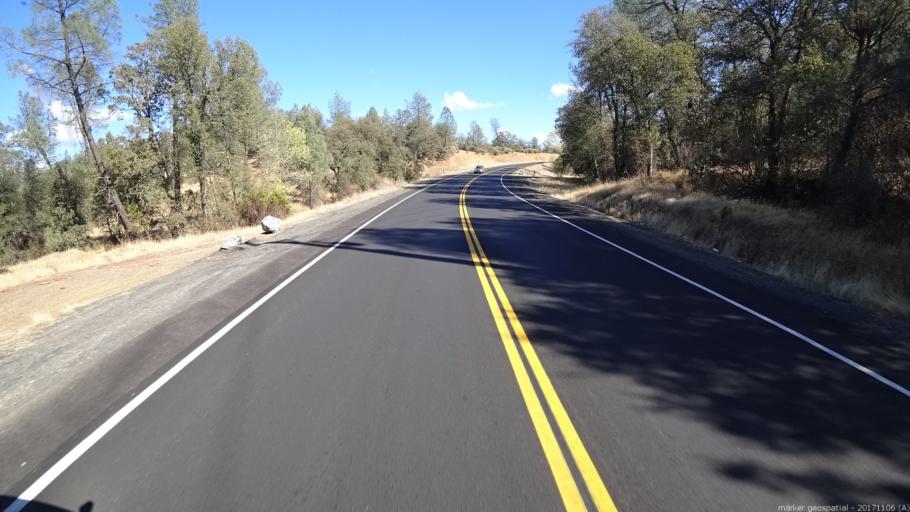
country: US
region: California
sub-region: Shasta County
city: Palo Cedro
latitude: 40.5929
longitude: -122.2941
